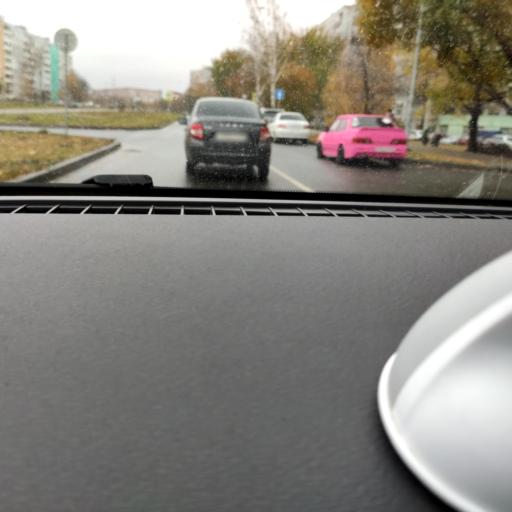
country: RU
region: Samara
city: Samara
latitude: 53.2511
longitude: 50.2475
